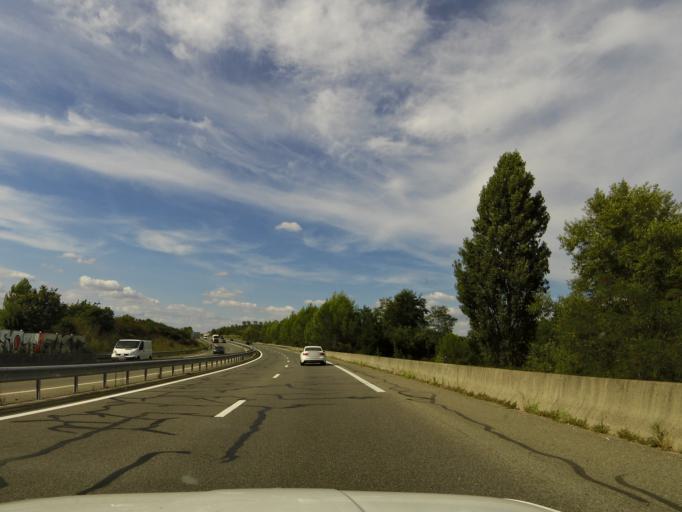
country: FR
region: Languedoc-Roussillon
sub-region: Departement du Gard
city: Vezenobres
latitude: 44.0300
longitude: 4.1485
